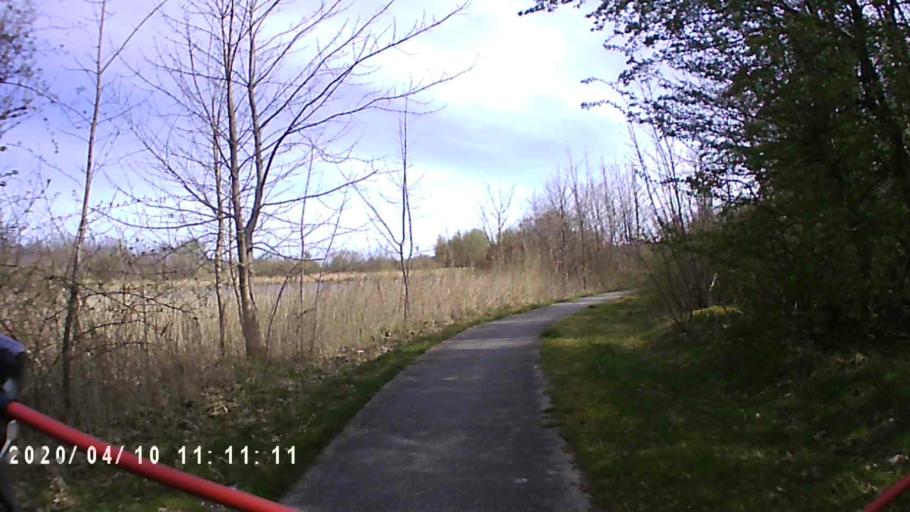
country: NL
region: Groningen
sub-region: Gemeente De Marne
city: Ulrum
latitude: 53.3934
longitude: 6.2514
